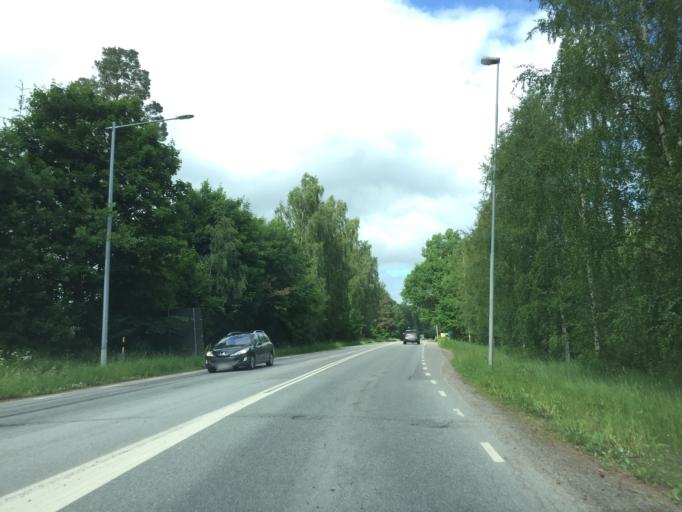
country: SE
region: OErebro
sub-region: Orebro Kommun
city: Orebro
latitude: 59.2389
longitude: 15.1536
